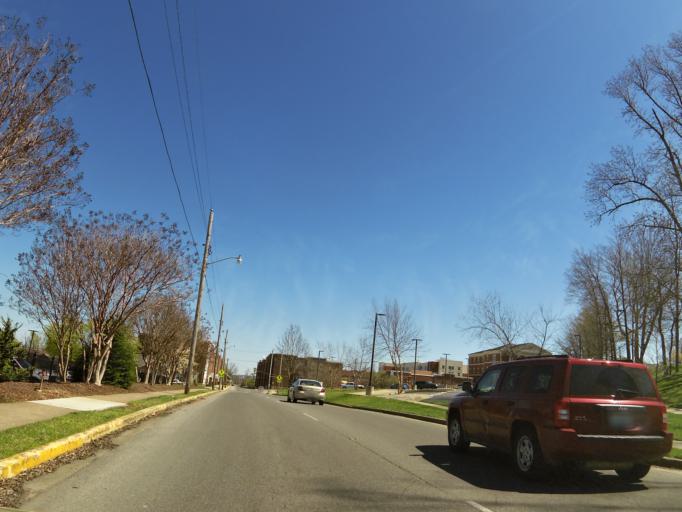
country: US
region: Kentucky
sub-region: Warren County
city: Bowling Green
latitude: 36.9893
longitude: -86.4537
